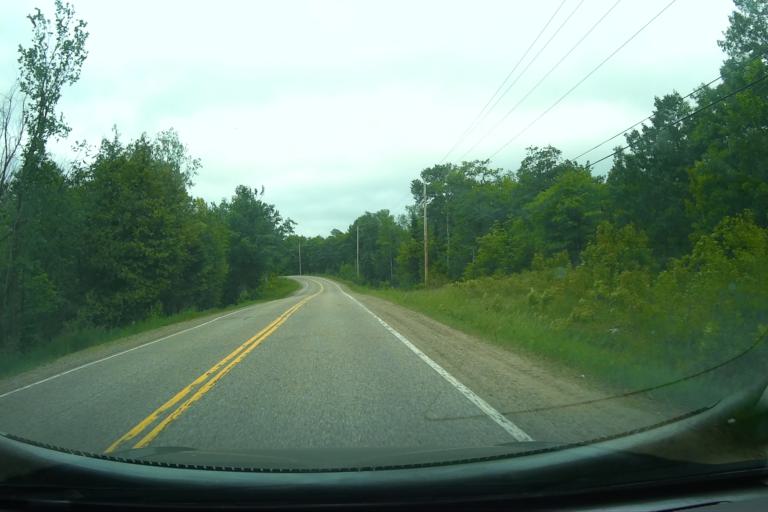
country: CA
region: Ontario
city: Pembroke
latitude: 45.4780
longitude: -77.2159
